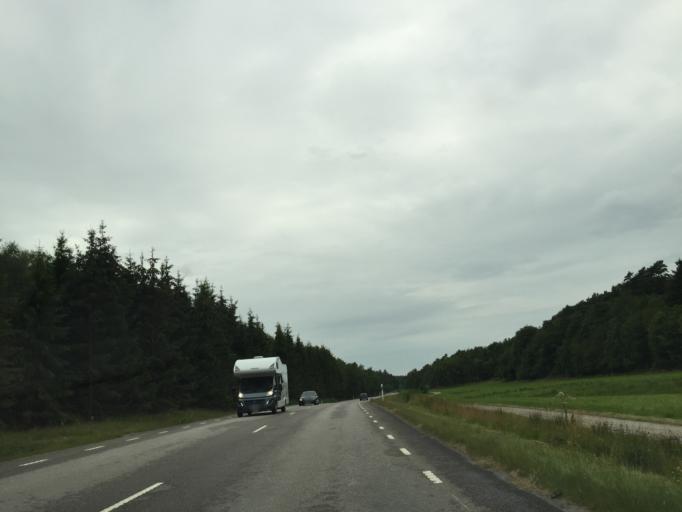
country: SE
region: Vaestra Goetaland
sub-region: Tjorns Kommun
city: Myggenas
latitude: 58.0233
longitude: 11.6895
